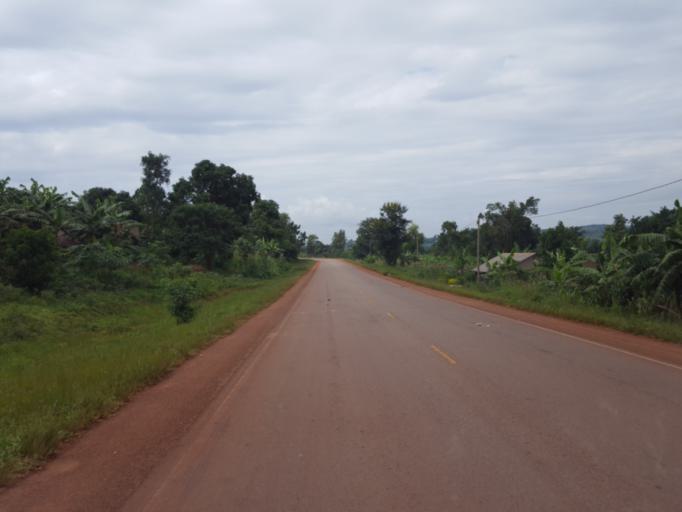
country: UG
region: Central Region
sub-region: Mityana District
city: Mityana
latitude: 0.6433
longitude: 32.0971
